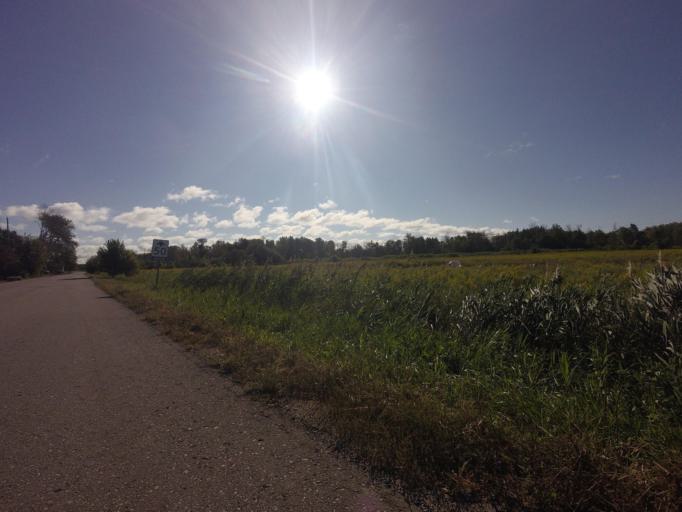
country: CA
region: Ontario
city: Bradford West Gwillimbury
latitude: 44.0482
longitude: -79.5699
